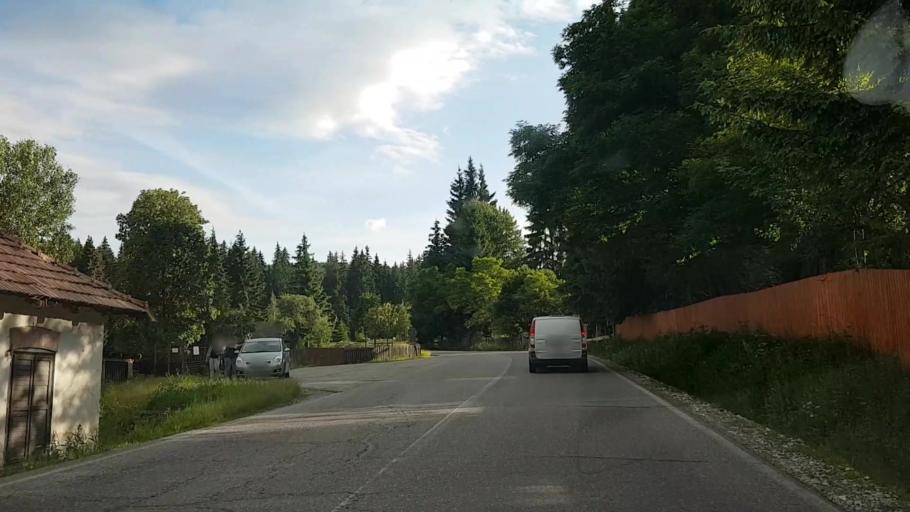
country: RO
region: Harghita
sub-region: Comuna Remetea
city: Remetea
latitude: 46.6758
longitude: 25.3616
